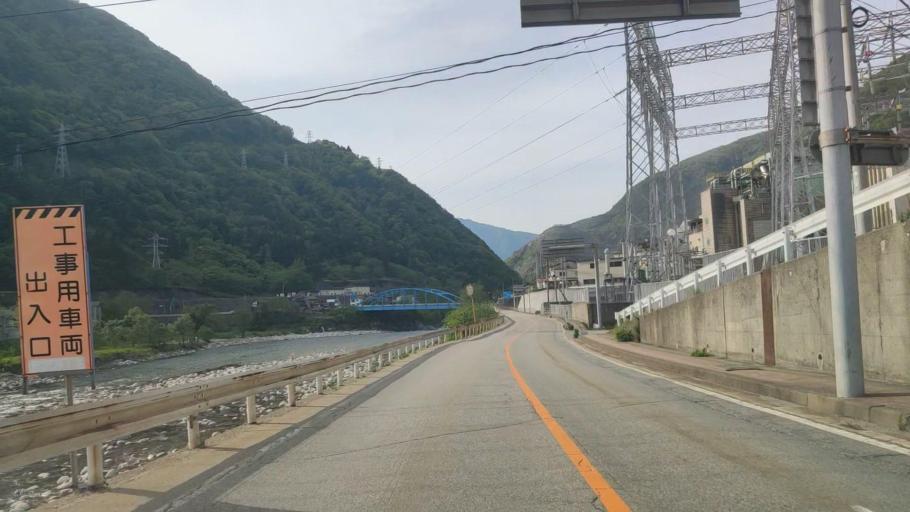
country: JP
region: Gifu
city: Takayama
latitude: 36.3371
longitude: 137.2981
